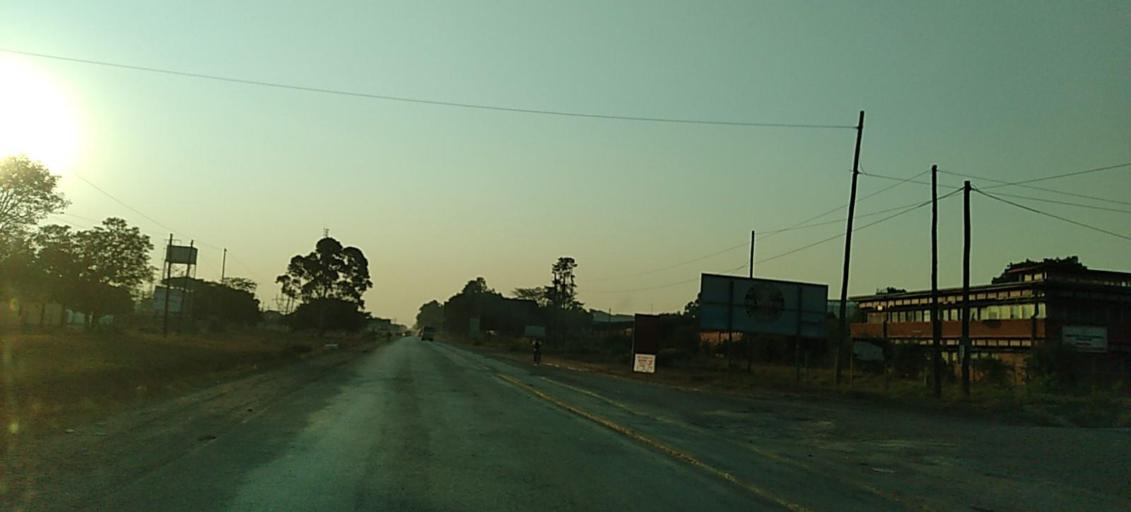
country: ZM
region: Copperbelt
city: Ndola
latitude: -13.0158
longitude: 28.6629
